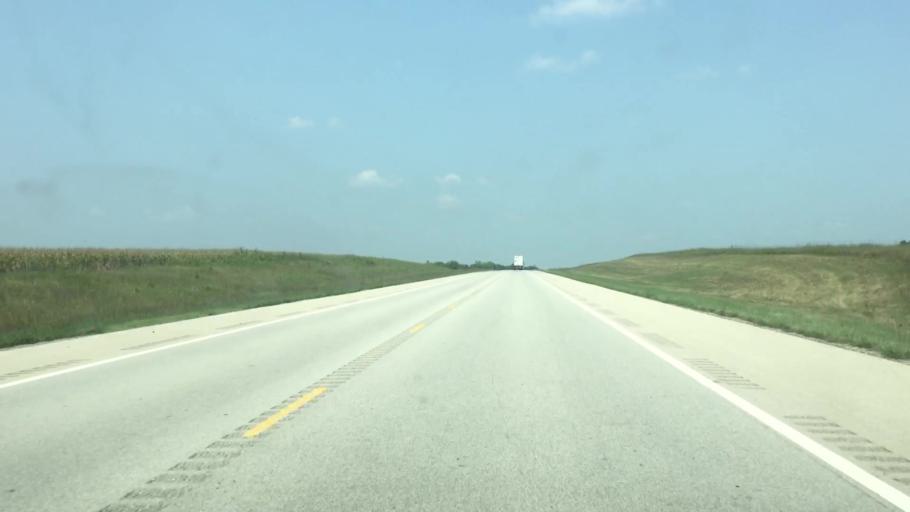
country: US
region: Kansas
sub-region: Allen County
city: Iola
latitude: 38.0575
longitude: -95.3804
